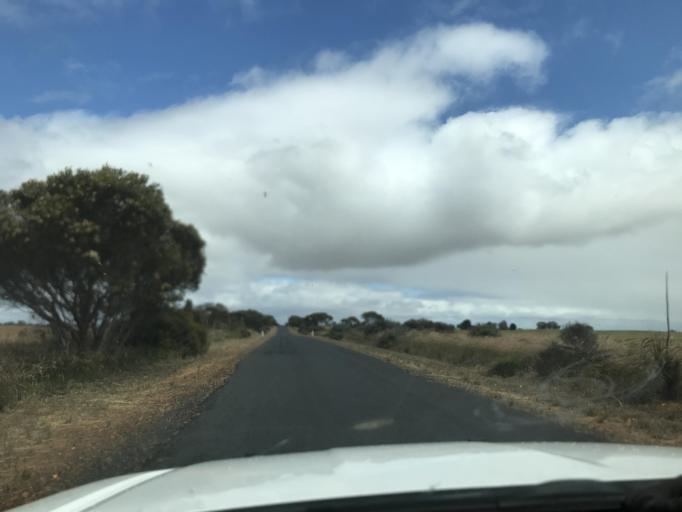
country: AU
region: South Australia
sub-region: Tatiara
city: Bordertown
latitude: -36.1370
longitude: 141.1979
